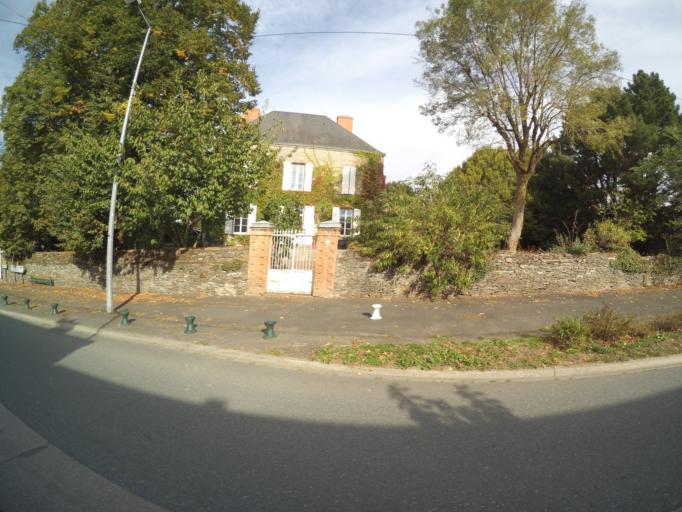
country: FR
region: Pays de la Loire
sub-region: Departement de Maine-et-Loire
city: Geste
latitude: 47.1803
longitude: -1.1055
